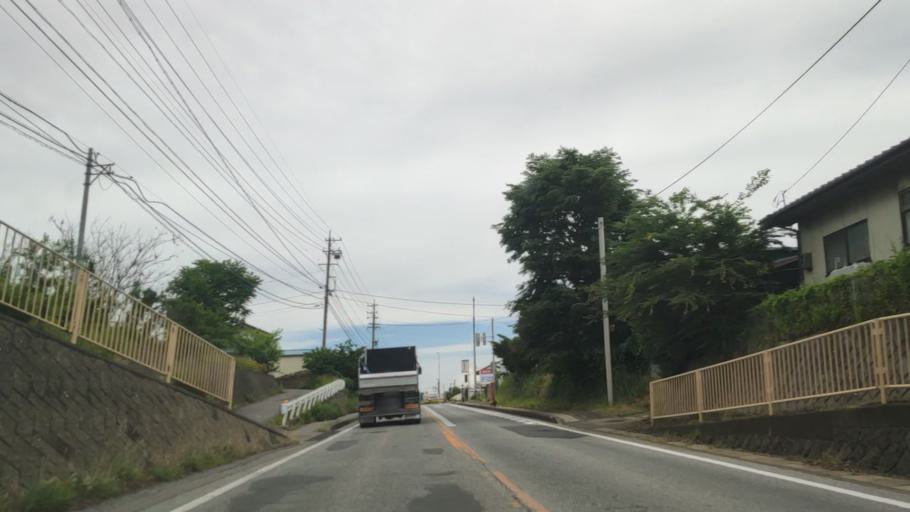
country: JP
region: Nagano
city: Komoro
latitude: 36.3424
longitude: 138.3873
